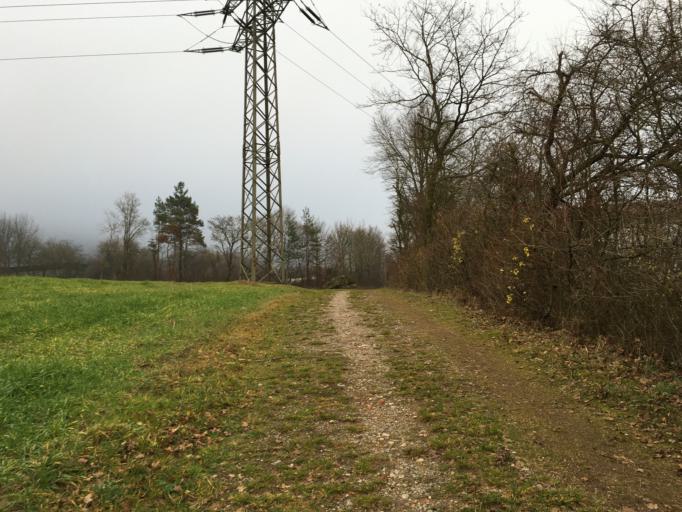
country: CH
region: Aargau
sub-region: Bezirk Zurzach
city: Bad Zurzach
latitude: 47.5711
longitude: 8.3361
